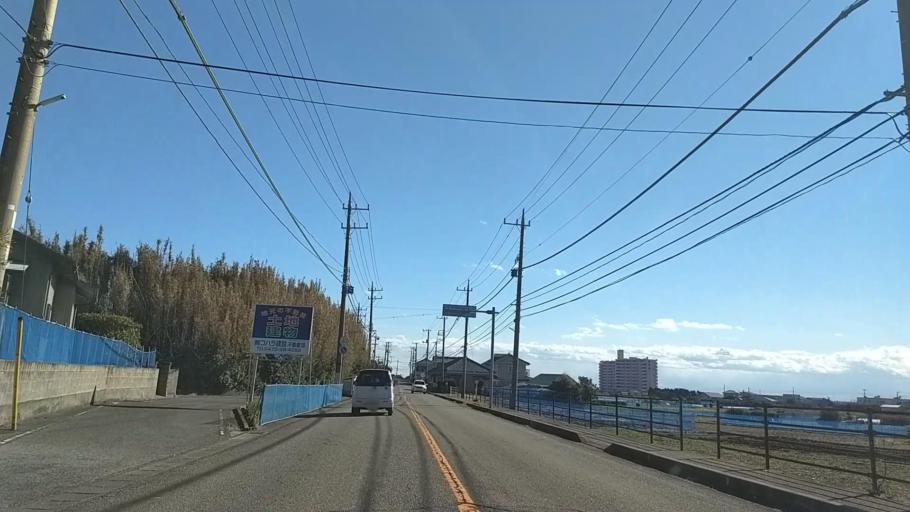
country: JP
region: Chiba
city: Tateyama
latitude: 34.9086
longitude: 139.8772
